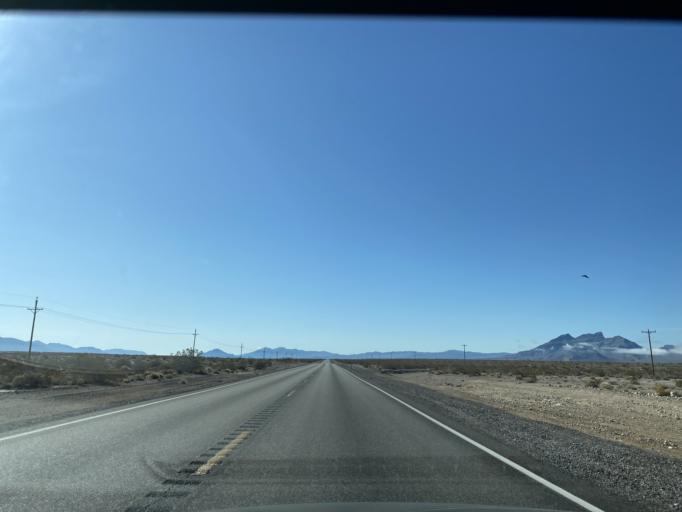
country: US
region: Nevada
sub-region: Nye County
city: Pahrump
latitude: 36.4765
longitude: -116.4216
